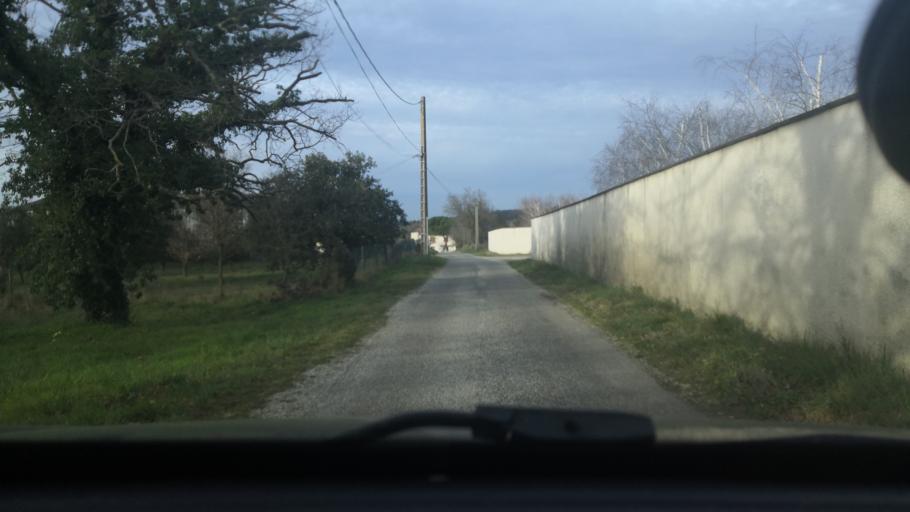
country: FR
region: Rhone-Alpes
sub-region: Departement de la Drome
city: Montelimar
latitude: 44.5413
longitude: 4.7735
